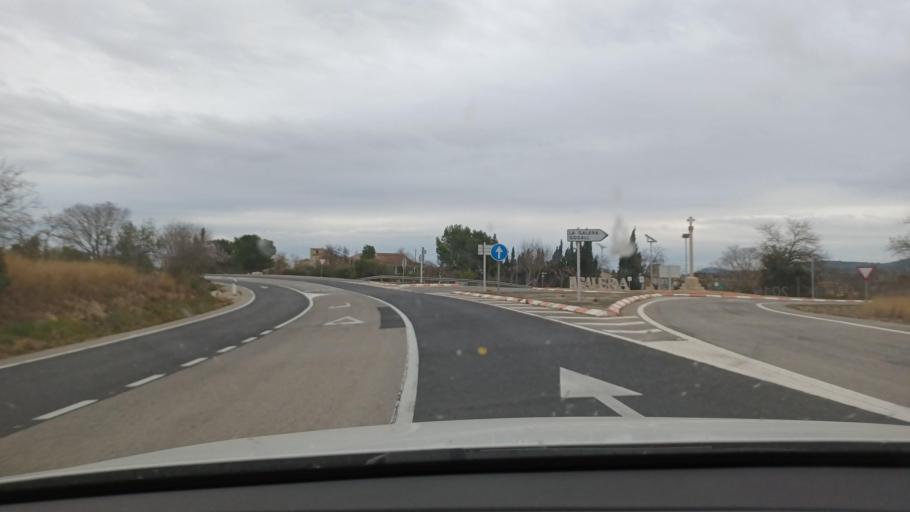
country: ES
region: Catalonia
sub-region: Provincia de Tarragona
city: Santa Barbara
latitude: 40.6779
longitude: 0.4571
